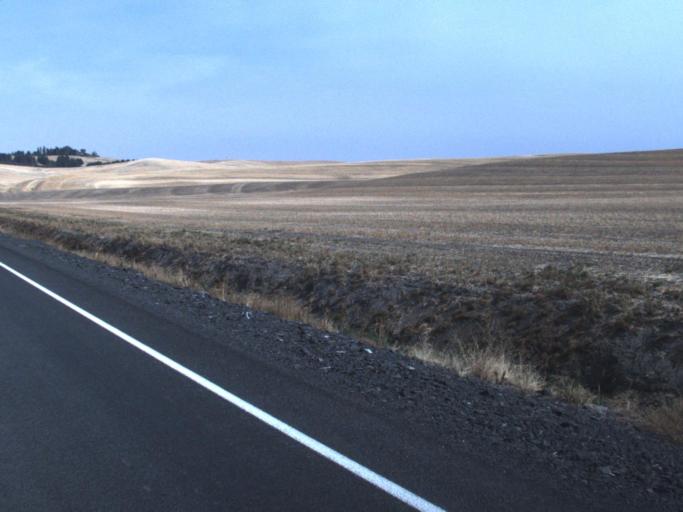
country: US
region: Washington
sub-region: Whitman County
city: Pullman
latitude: 46.7882
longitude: -117.1478
